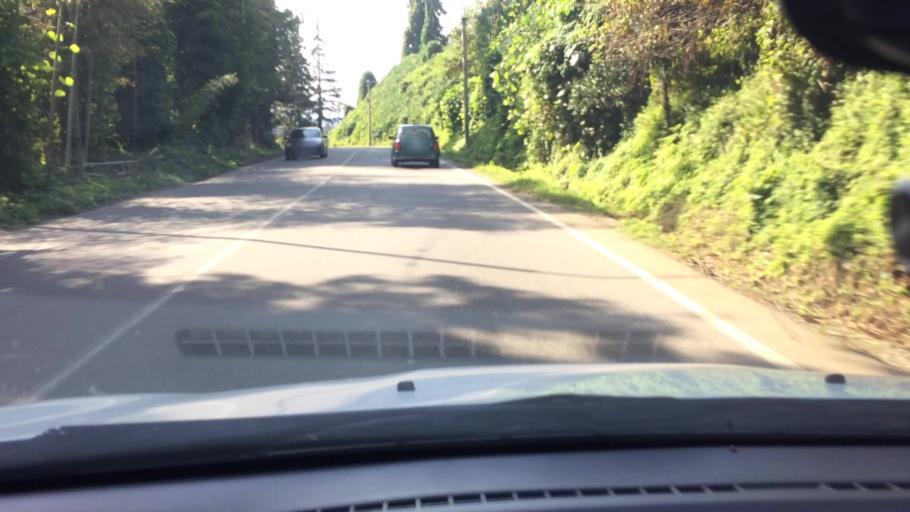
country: GE
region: Ajaria
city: Kobuleti
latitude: 41.7515
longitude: 41.7447
